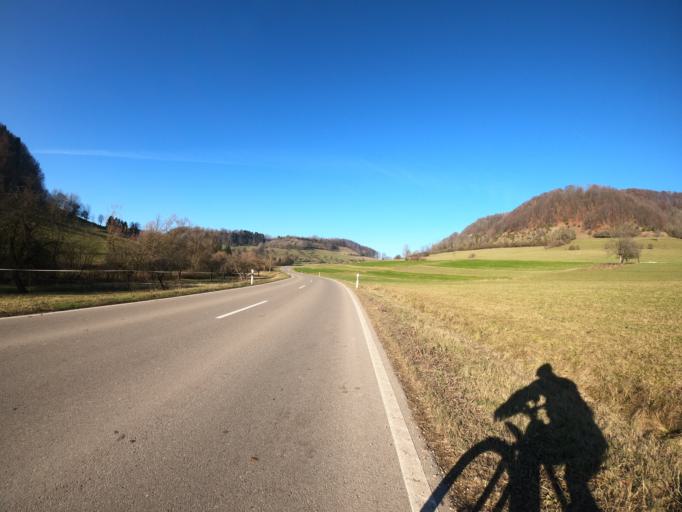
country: DE
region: Baden-Wuerttemberg
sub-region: Regierungsbezirk Stuttgart
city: Eschenbach
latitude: 48.6207
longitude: 9.6784
